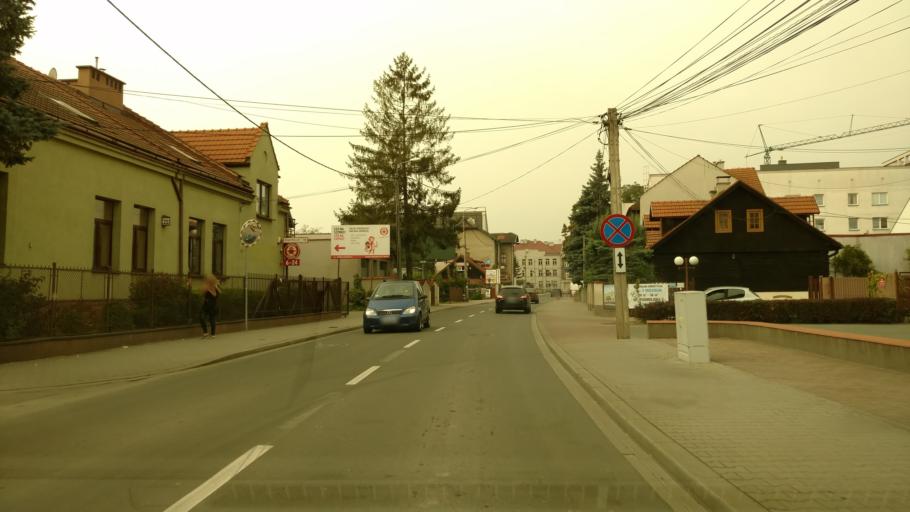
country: PL
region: Lesser Poland Voivodeship
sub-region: Krakow
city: Krakow
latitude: 50.0882
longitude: 19.9608
